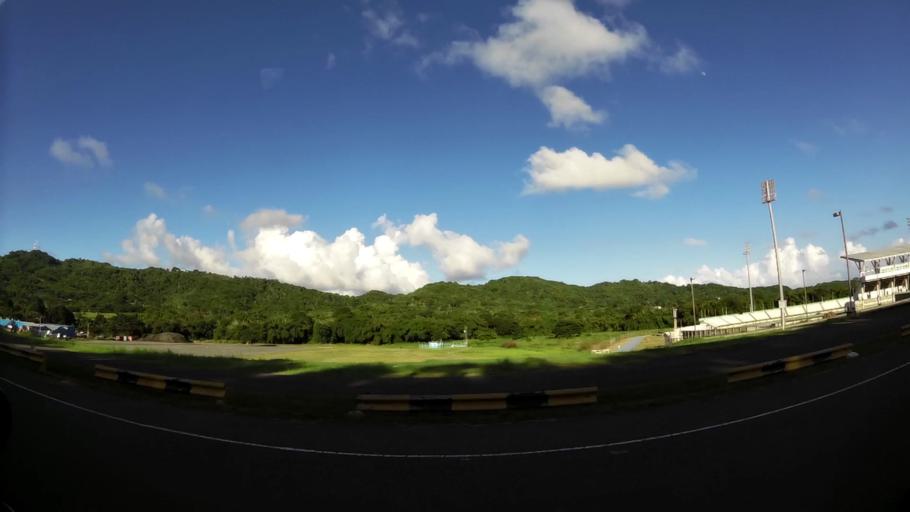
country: TT
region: Tobago
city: Scarborough
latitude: 11.1823
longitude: -60.7188
